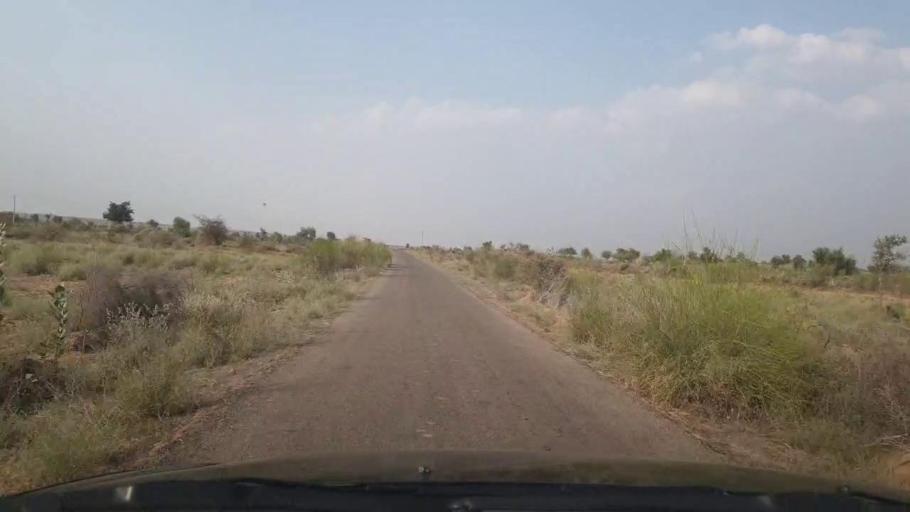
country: PK
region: Sindh
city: Islamkot
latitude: 25.0505
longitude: 70.5586
